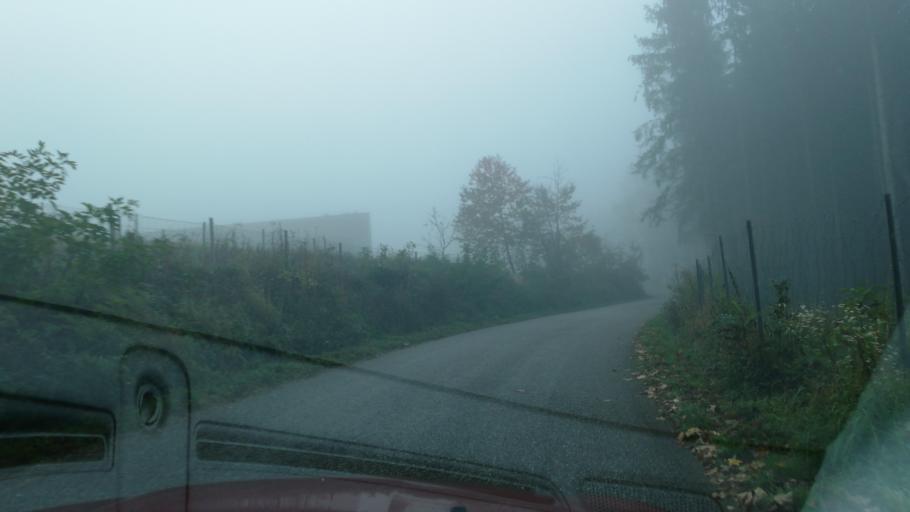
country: AT
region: Upper Austria
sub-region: Politischer Bezirk Grieskirchen
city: Bad Schallerbach
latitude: 48.2063
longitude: 13.8957
